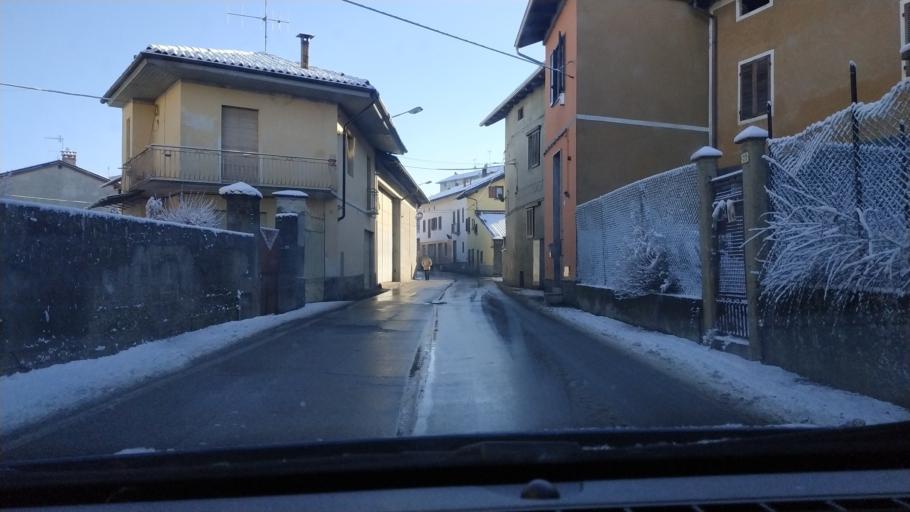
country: IT
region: Piedmont
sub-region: Provincia di Torino
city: Vische
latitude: 45.3341
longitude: 7.9477
